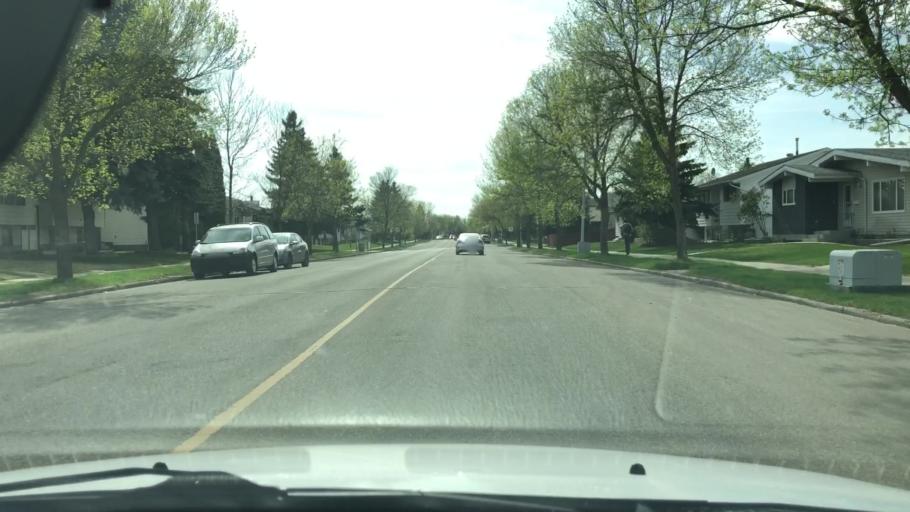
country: CA
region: Alberta
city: Edmonton
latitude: 53.6019
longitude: -113.5200
